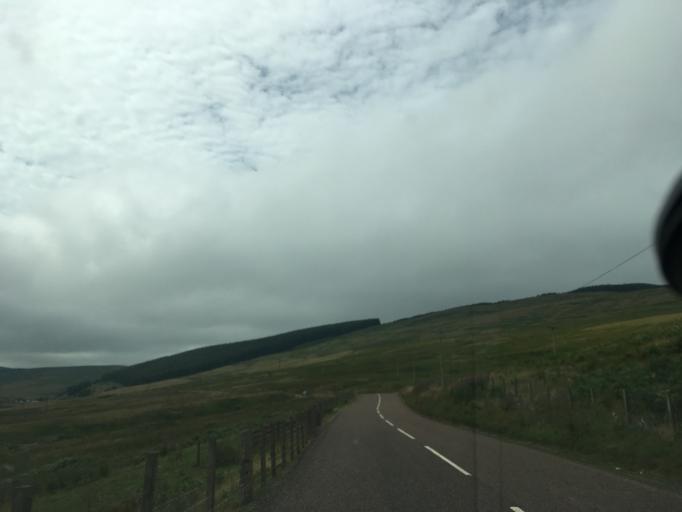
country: GB
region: Scotland
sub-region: South Lanarkshire
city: Douglas
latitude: 55.4775
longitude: -3.7139
